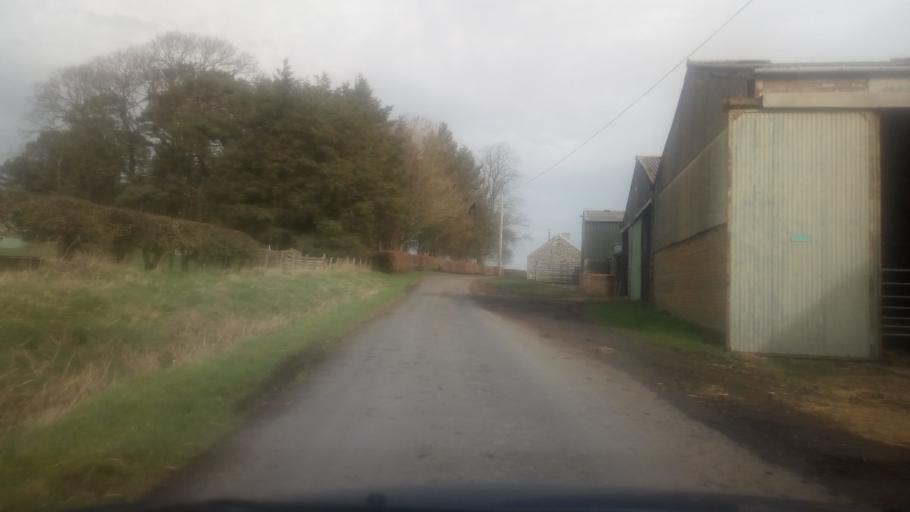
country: GB
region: Scotland
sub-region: The Scottish Borders
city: Hawick
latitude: 55.4330
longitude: -2.6968
